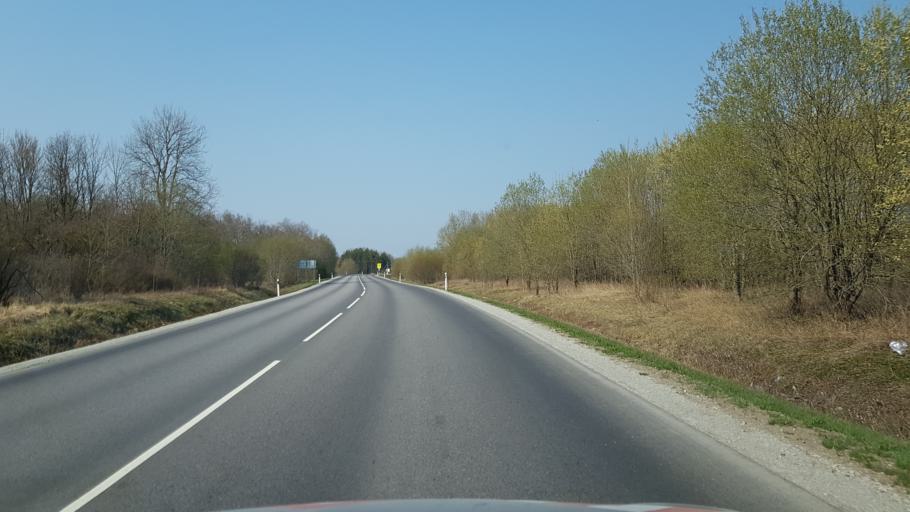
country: EE
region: Harju
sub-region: Paldiski linn
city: Paldiski
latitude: 59.3329
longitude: 24.1027
